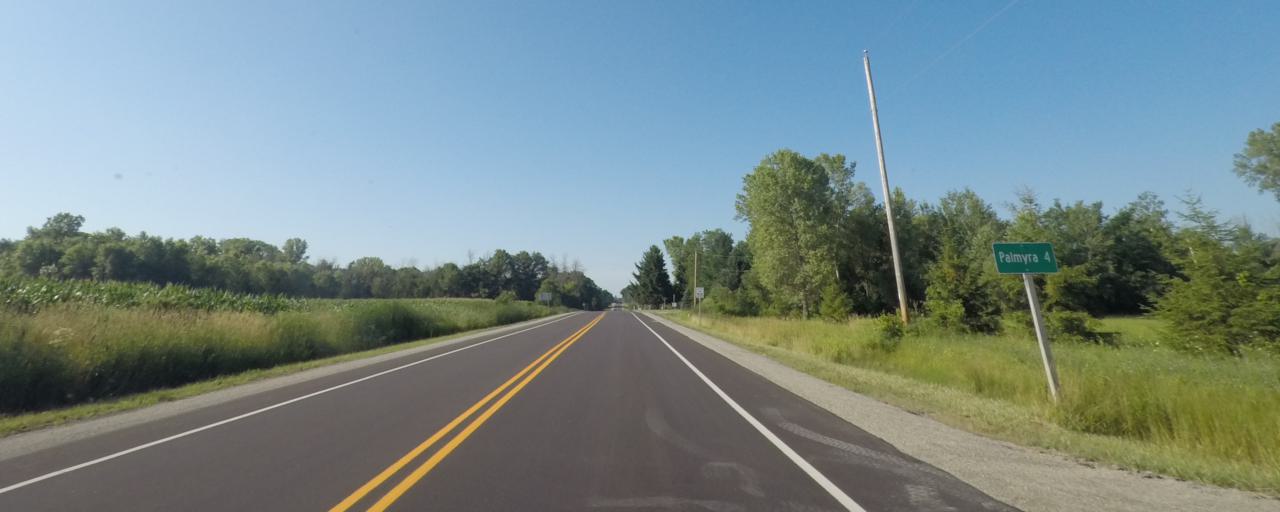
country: US
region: Wisconsin
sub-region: Jefferson County
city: Palmyra
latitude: 42.9352
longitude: -88.5867
